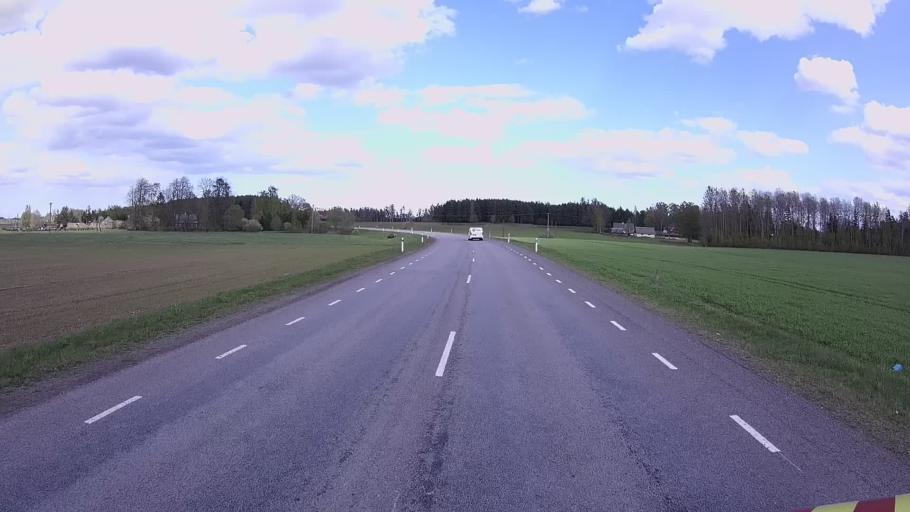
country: EE
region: Tartu
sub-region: Alatskivi vald
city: Kallaste
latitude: 58.5162
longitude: 26.9953
